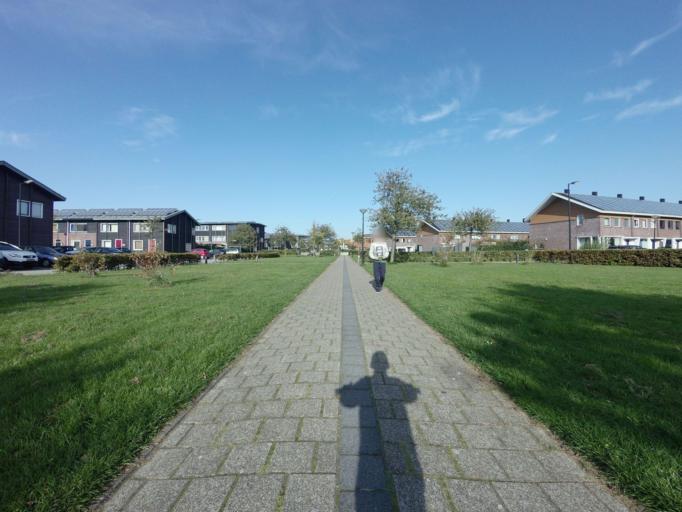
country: NL
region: North Holland
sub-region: Gemeente Alkmaar
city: Alkmaar
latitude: 52.6526
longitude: 4.7702
